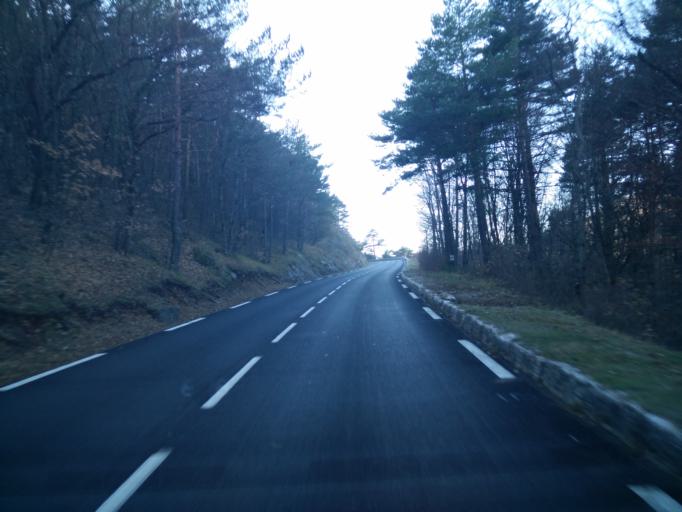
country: FR
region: Provence-Alpes-Cote d'Azur
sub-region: Departement des Alpes-Maritimes
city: Saint-Vallier-de-Thiey
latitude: 43.7162
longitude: 6.8594
